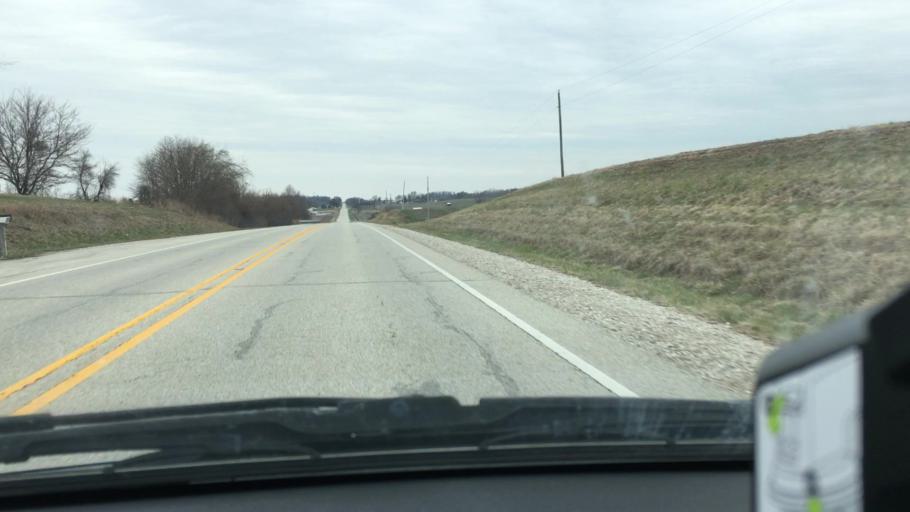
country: US
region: Indiana
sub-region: Greene County
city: Bloomfield
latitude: 38.9646
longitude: -87.0158
